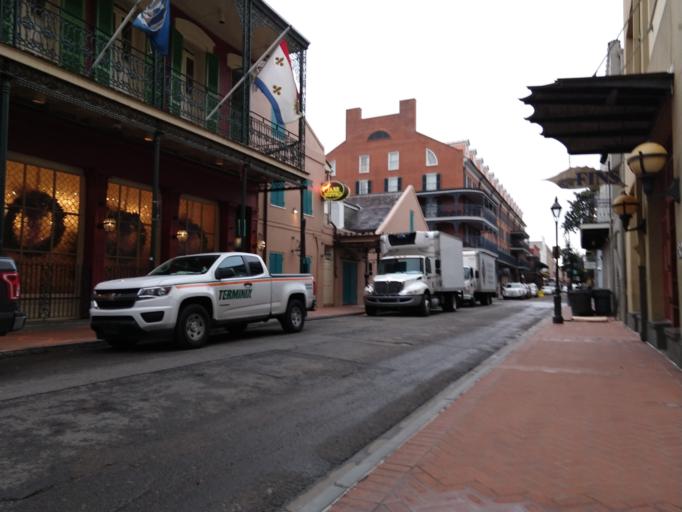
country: US
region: Louisiana
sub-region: Orleans Parish
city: New Orleans
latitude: 29.9557
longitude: -90.0688
